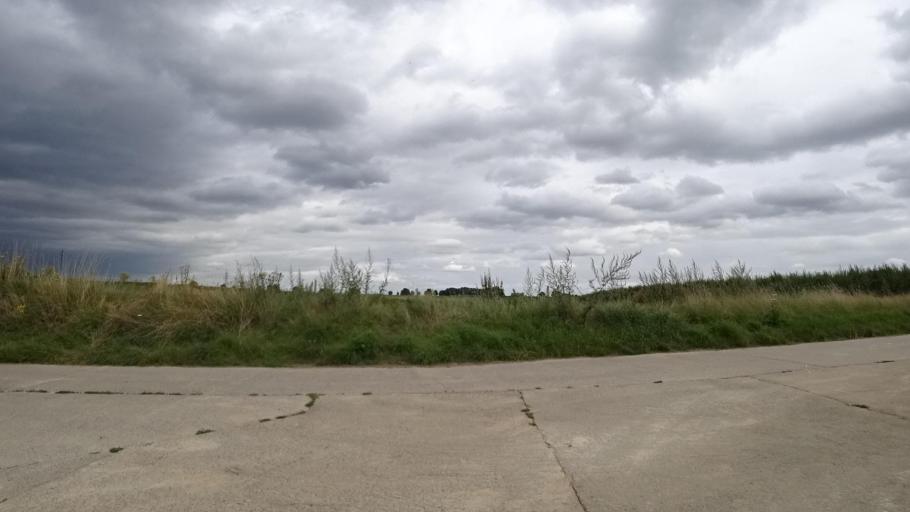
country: BE
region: Wallonia
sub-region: Province du Brabant Wallon
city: Mont-Saint-Guibert
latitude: 50.6457
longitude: 4.6317
